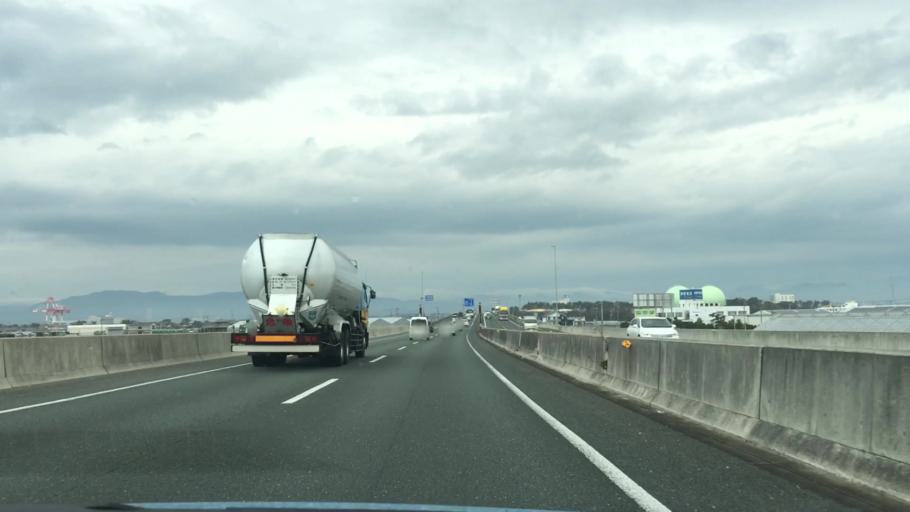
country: JP
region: Aichi
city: Toyohashi
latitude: 34.7494
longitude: 137.3356
